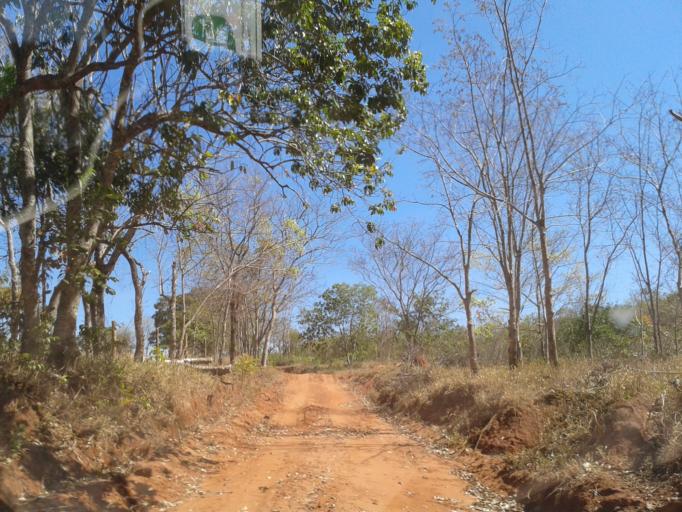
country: BR
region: Minas Gerais
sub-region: Ituiutaba
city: Ituiutaba
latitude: -19.0988
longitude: -49.2996
